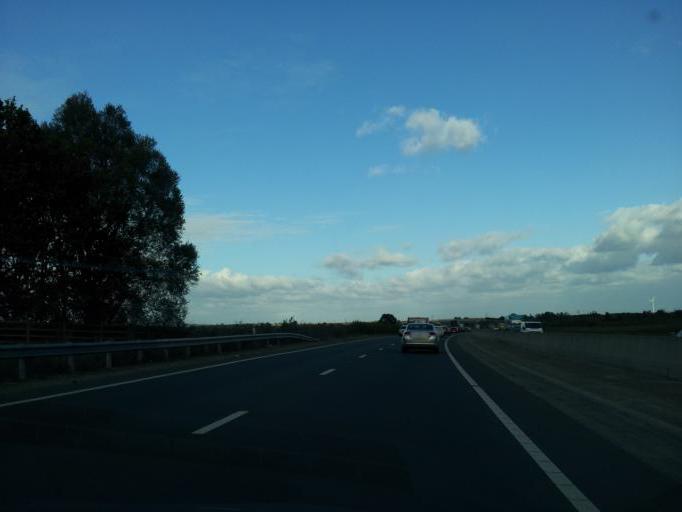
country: GB
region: England
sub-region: Central Bedfordshire
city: Lidlington
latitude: 52.0487
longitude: -0.5850
